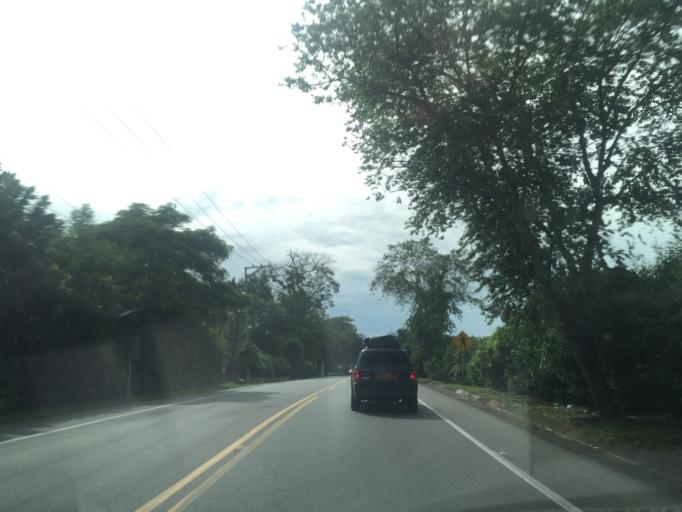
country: CO
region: Quindio
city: La Tebaida
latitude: 4.4687
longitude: -75.7684
